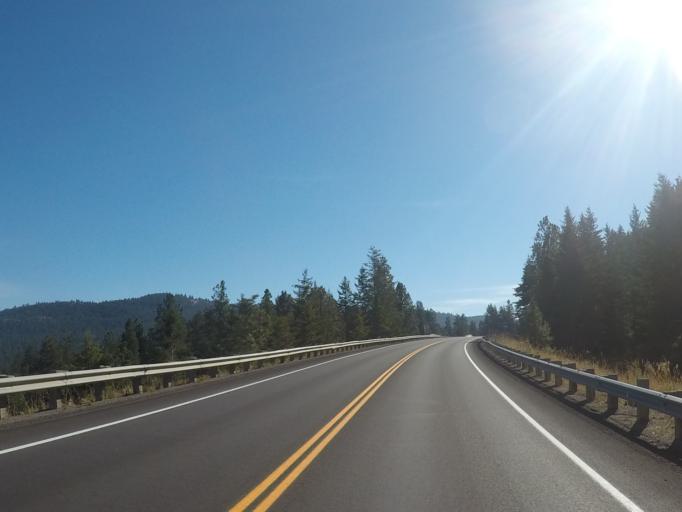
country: US
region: Montana
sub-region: Lake County
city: Polson
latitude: 47.8065
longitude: -114.2387
